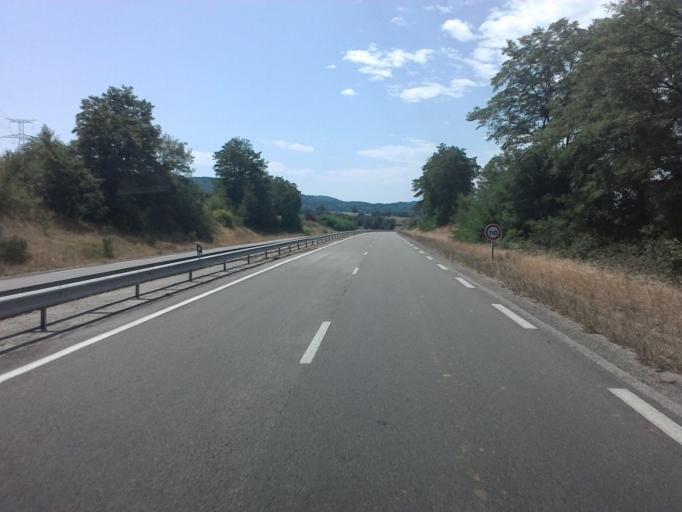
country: FR
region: Bourgogne
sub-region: Departement de Saone-et-Loire
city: Cuiseaux
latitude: 46.5135
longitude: 5.3883
